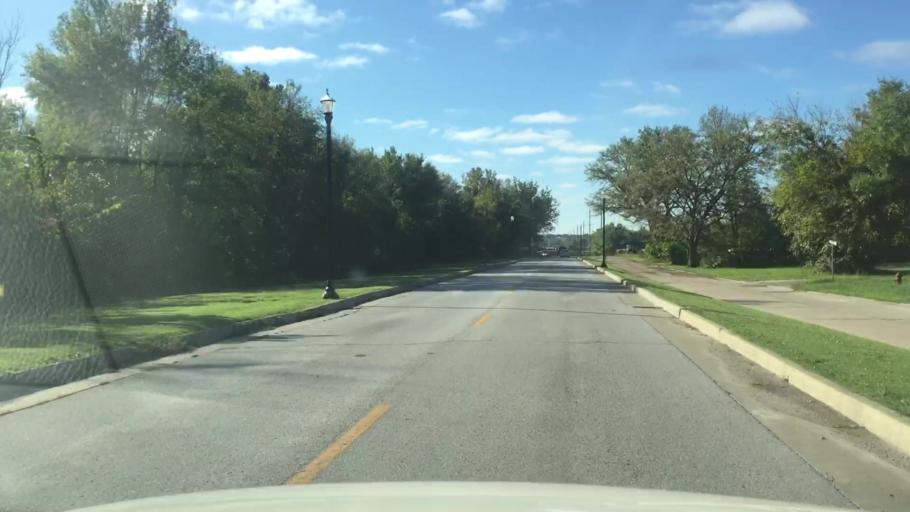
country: US
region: Missouri
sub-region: Howard County
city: New Franklin
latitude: 39.0116
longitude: -92.7378
